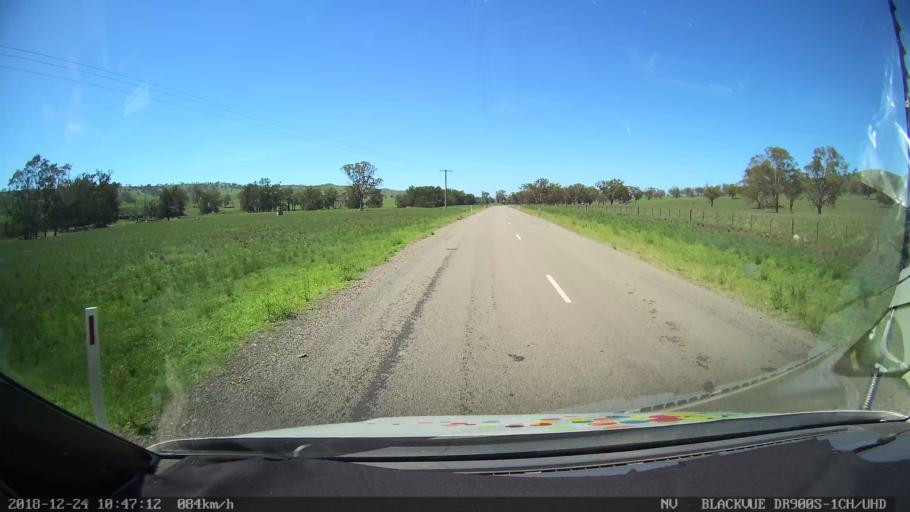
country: AU
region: New South Wales
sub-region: Upper Hunter Shire
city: Merriwa
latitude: -31.9216
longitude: 150.4294
